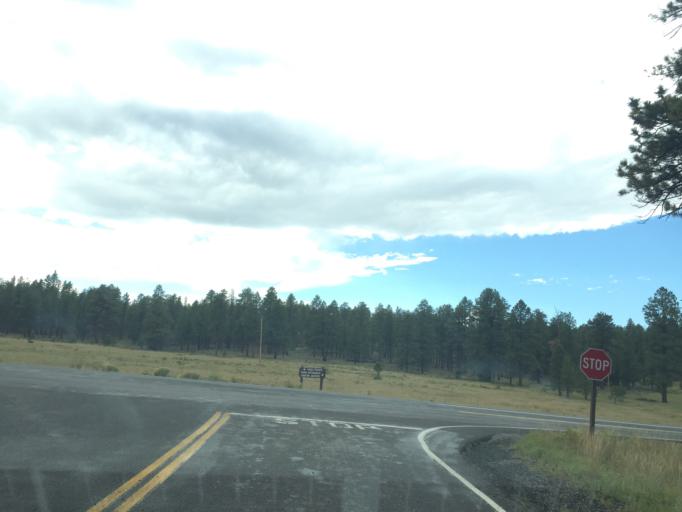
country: US
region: Utah
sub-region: Garfield County
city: Panguitch
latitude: 37.6271
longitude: -112.1719
